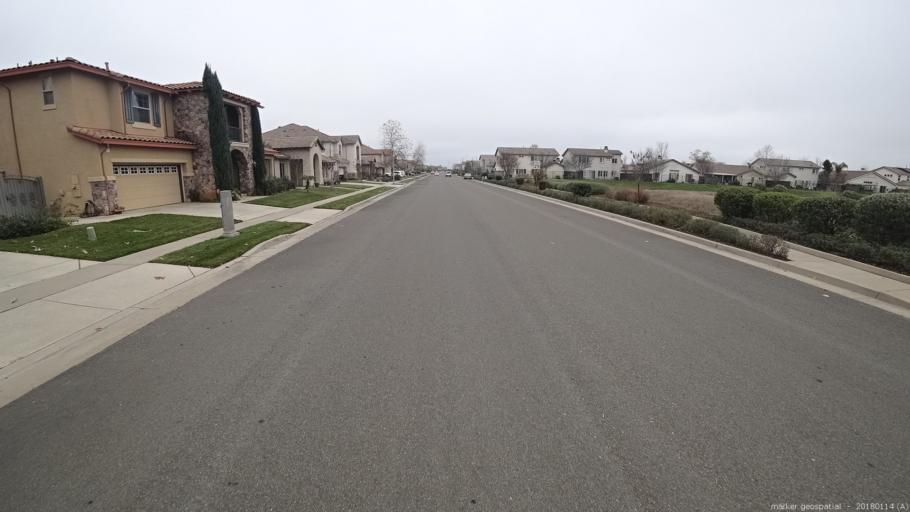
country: US
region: California
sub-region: Sacramento County
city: Rancho Cordova
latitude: 38.5425
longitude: -121.2386
